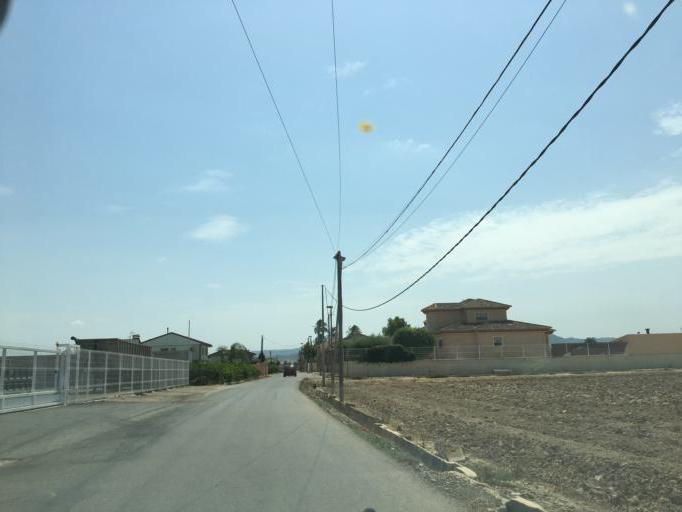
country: ES
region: Murcia
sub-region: Murcia
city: Santomera
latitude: 38.0347
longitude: -1.0535
